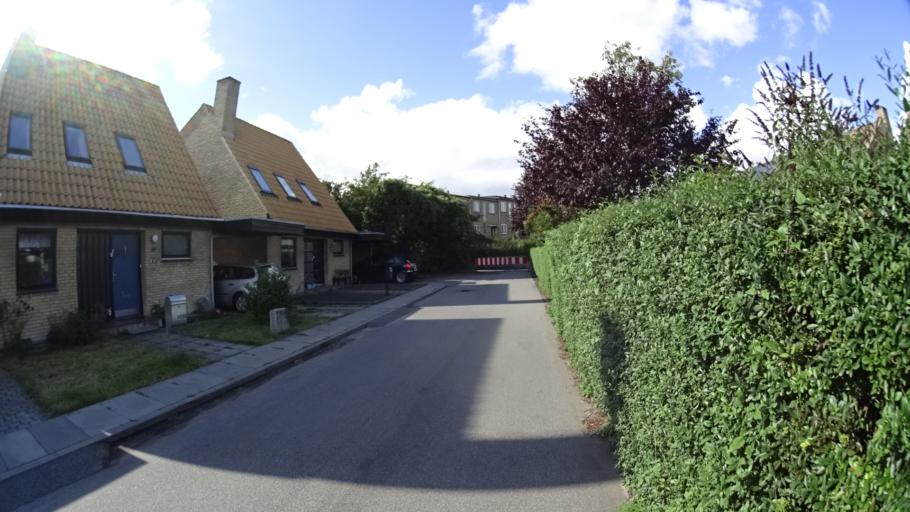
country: DK
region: Central Jutland
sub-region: Arhus Kommune
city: Arhus
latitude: 56.1629
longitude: 10.1740
